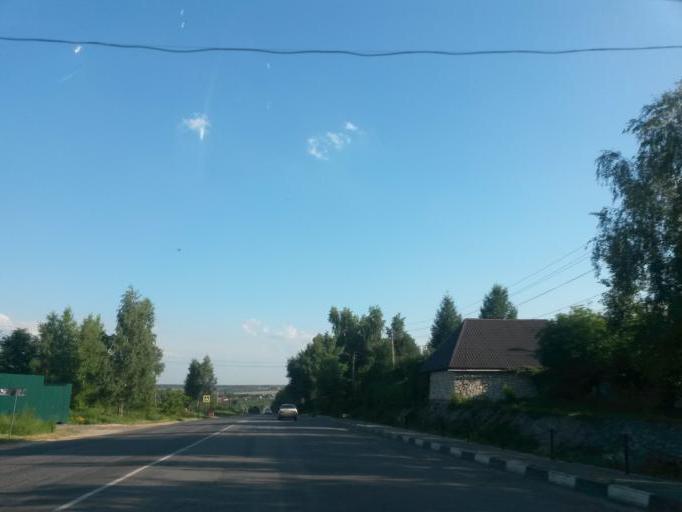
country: RU
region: Moskovskaya
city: Gorki-Leninskiye
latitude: 55.4975
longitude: 37.7803
